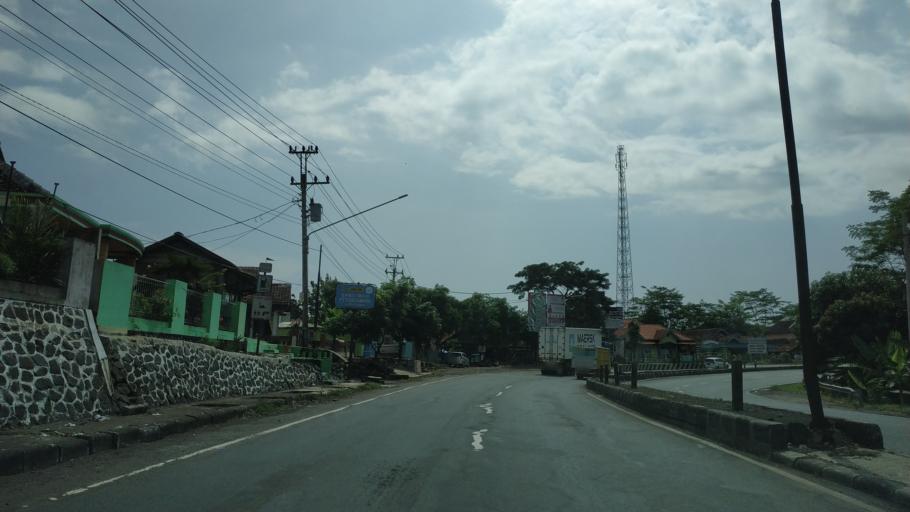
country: ID
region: Central Java
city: Pekalongan
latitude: -6.9452
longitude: 109.8185
